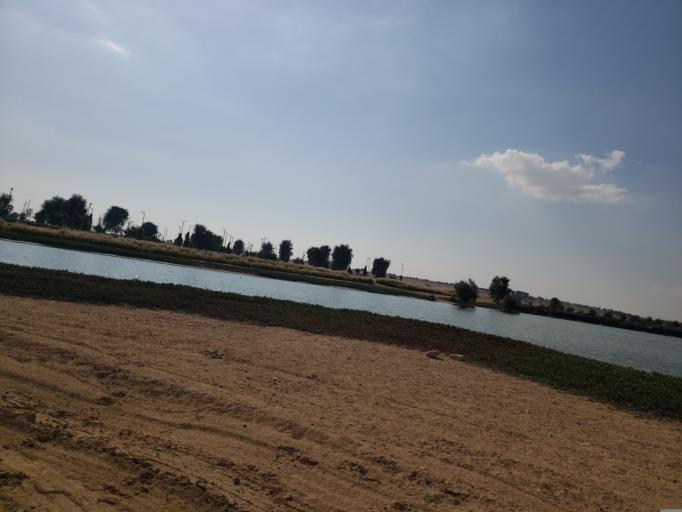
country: AE
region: Dubai
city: Dubai
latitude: 24.8562
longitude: 55.2467
